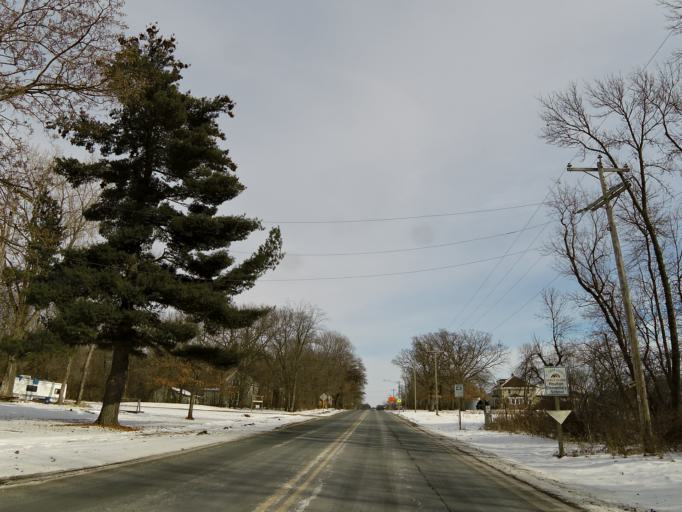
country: US
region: Minnesota
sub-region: Washington County
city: Stillwater
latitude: 45.0607
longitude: -92.7907
